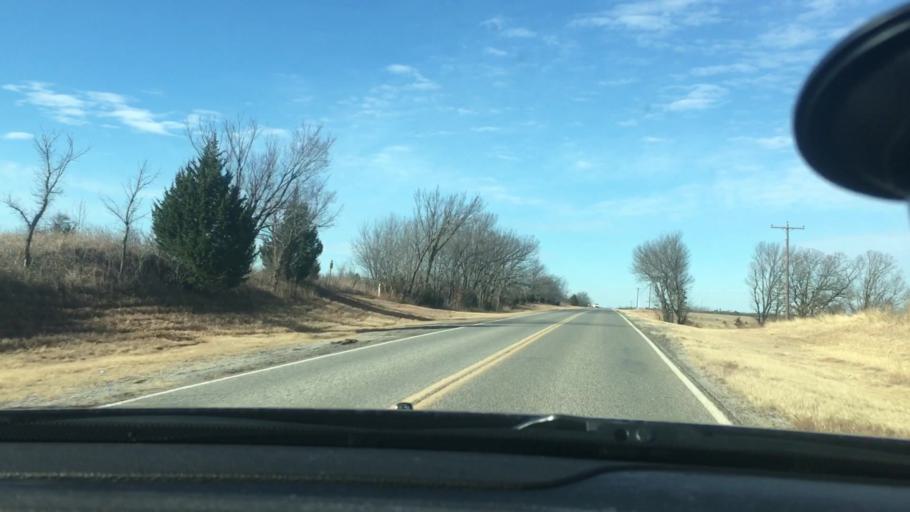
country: US
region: Oklahoma
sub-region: Seminole County
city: Konawa
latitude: 34.9859
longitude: -96.9007
